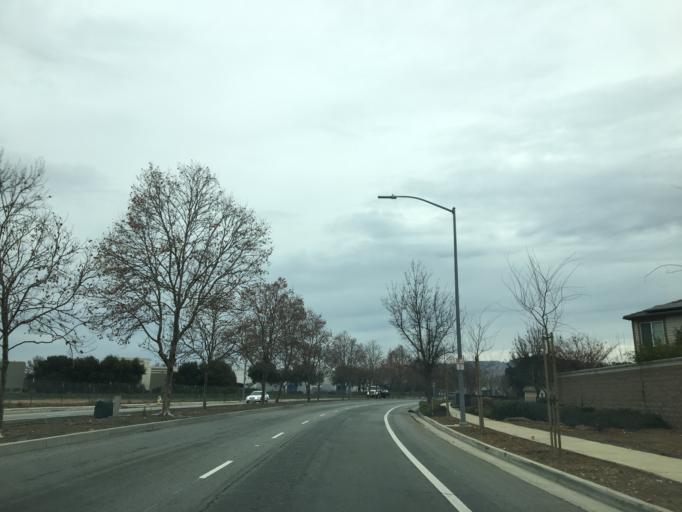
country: US
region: California
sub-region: Santa Clara County
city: Morgan Hill
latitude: 37.1360
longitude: -121.6543
